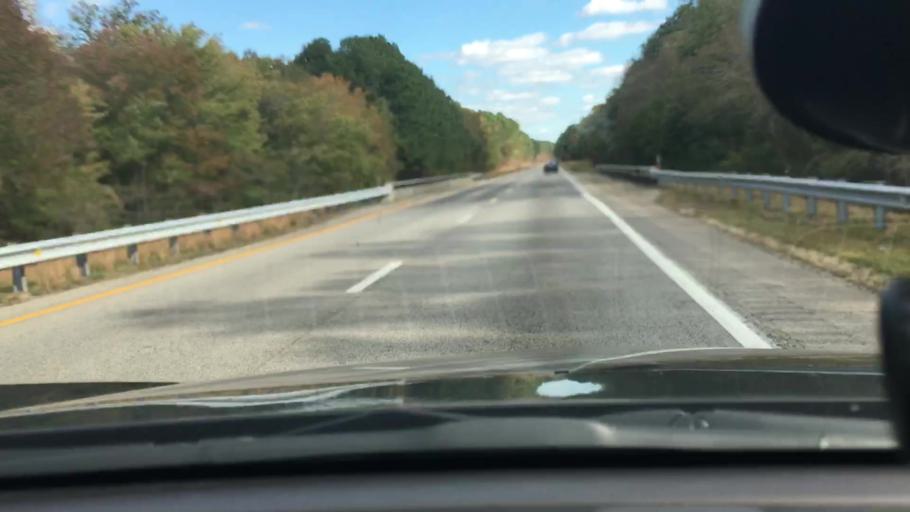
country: US
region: North Carolina
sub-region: Wake County
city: Zebulon
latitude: 35.7948
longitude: -78.1703
